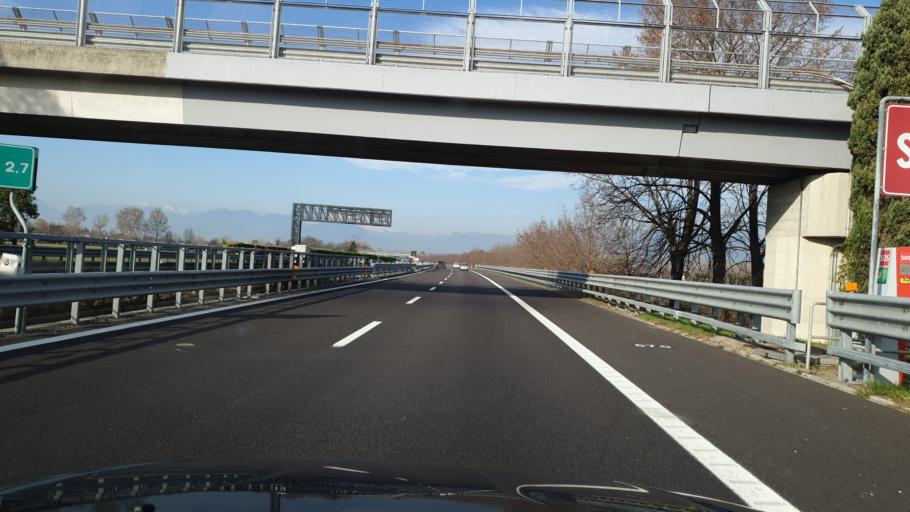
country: IT
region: Veneto
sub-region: Provincia di Vicenza
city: Vigardolo
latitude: 45.6253
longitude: 11.5928
